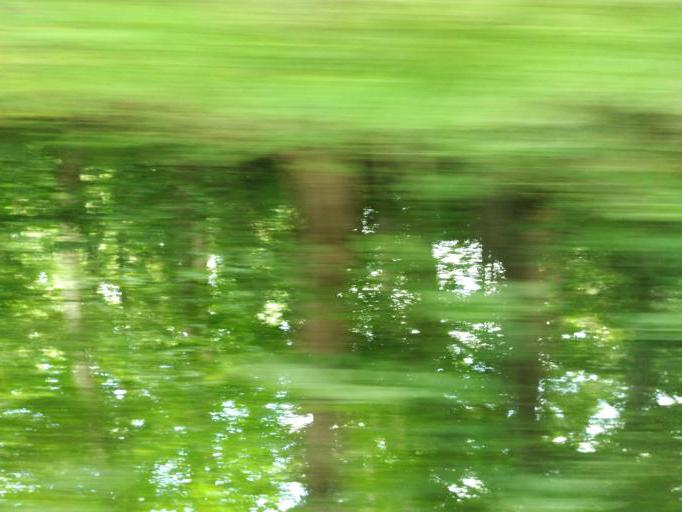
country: US
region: Maryland
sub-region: Anne Arundel County
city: Deale
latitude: 38.8094
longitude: -76.5763
